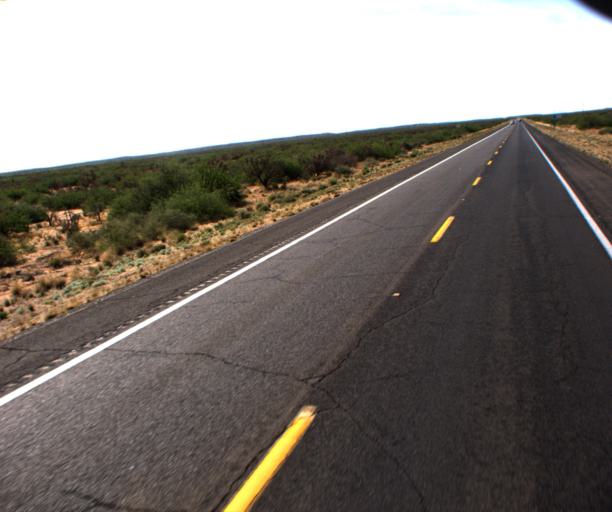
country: US
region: Arizona
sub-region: Graham County
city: Swift Trail Junction
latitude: 32.6784
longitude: -109.7056
